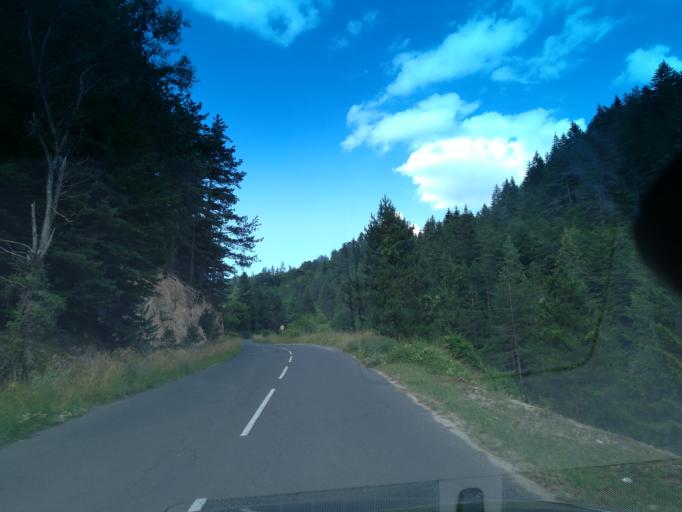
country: BG
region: Smolyan
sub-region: Obshtina Smolyan
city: Smolyan
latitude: 41.6503
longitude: 24.7702
